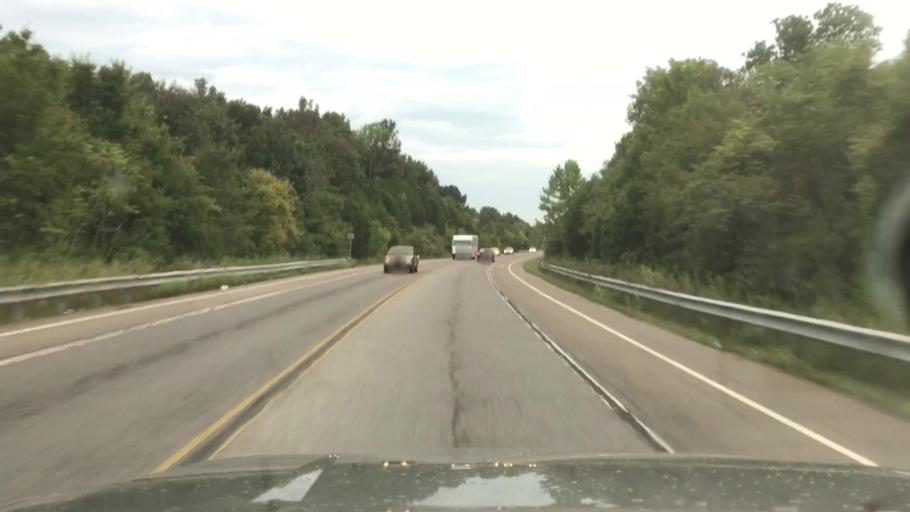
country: US
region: Tennessee
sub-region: Rutherford County
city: La Vergne
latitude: 36.0987
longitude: -86.6251
